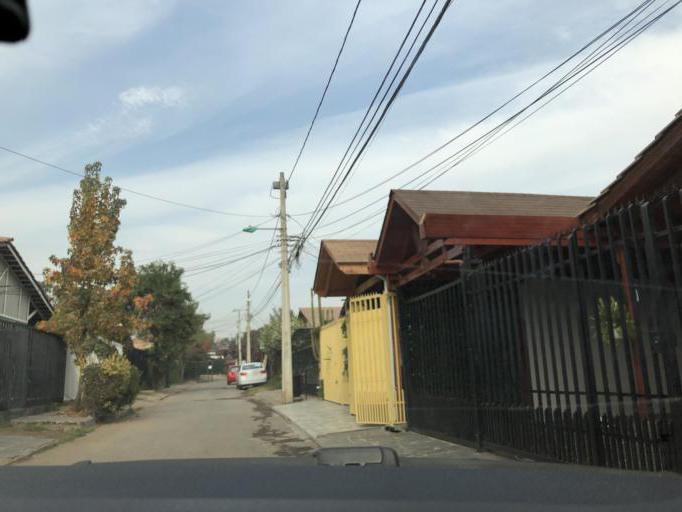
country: CL
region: Santiago Metropolitan
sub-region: Provincia de Cordillera
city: Puente Alto
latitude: -33.5579
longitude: -70.5550
